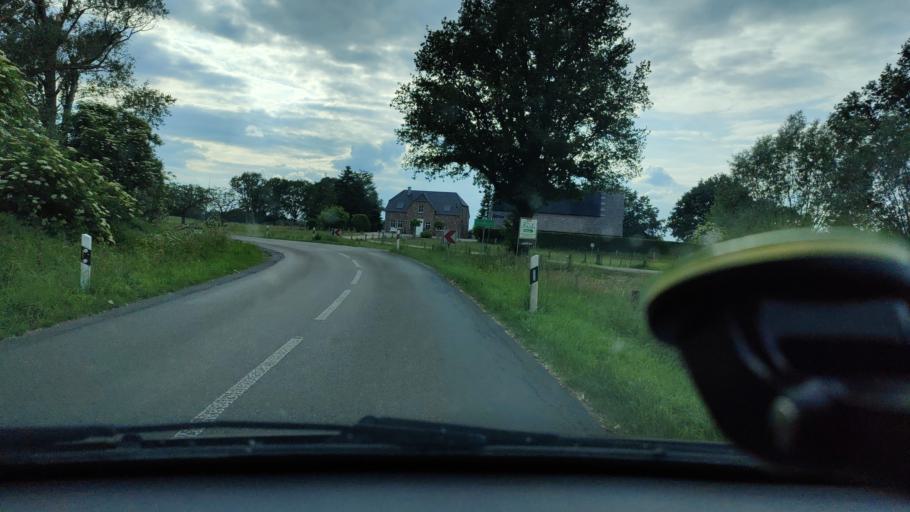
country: DE
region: North Rhine-Westphalia
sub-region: Regierungsbezirk Dusseldorf
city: Weeze
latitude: 51.6263
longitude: 6.1686
